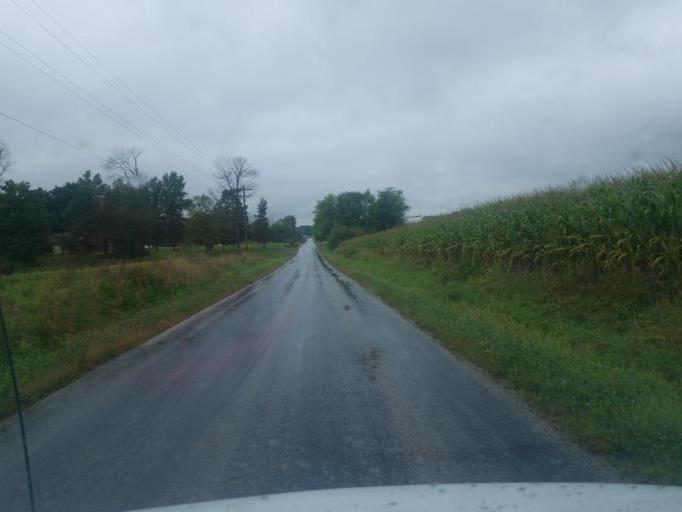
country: US
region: Ohio
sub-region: Wayne County
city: West Salem
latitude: 40.9378
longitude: -82.0744
